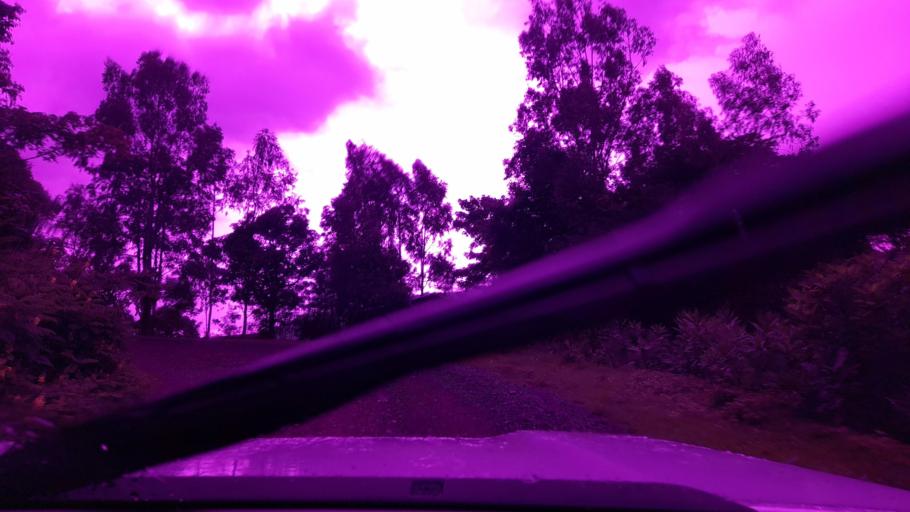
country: ET
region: Oromiya
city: Metu
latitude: 8.4434
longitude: 35.6244
